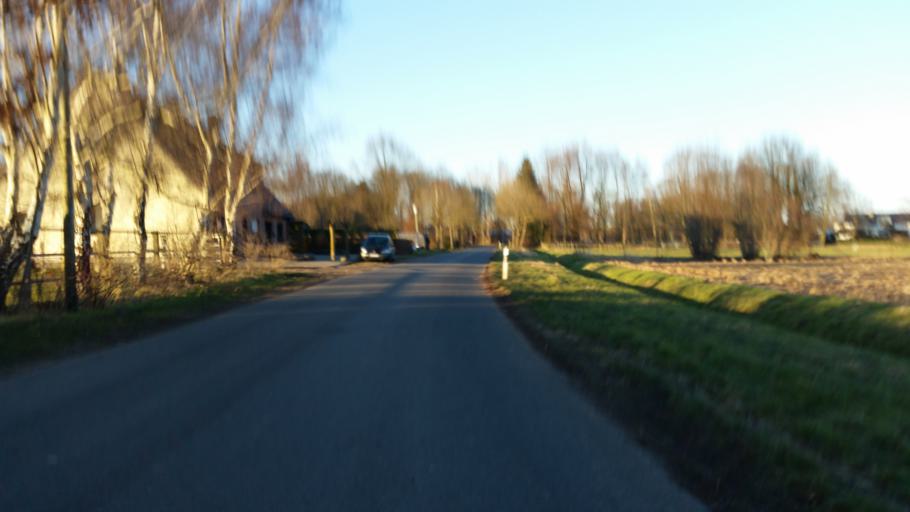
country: DE
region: North Rhine-Westphalia
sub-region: Regierungsbezirk Munster
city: Neuenkirchen
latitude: 52.2765
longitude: 7.3944
